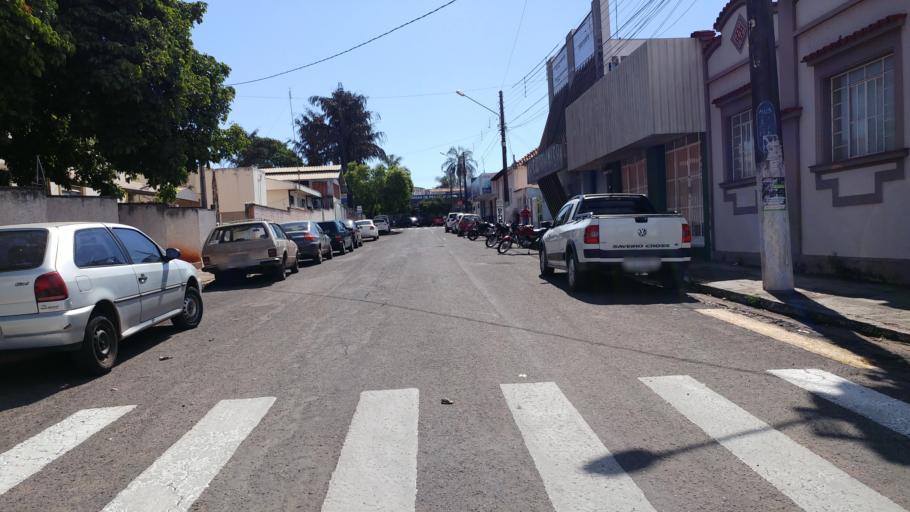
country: BR
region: Sao Paulo
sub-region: Paraguacu Paulista
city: Paraguacu Paulista
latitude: -22.4143
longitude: -50.5781
